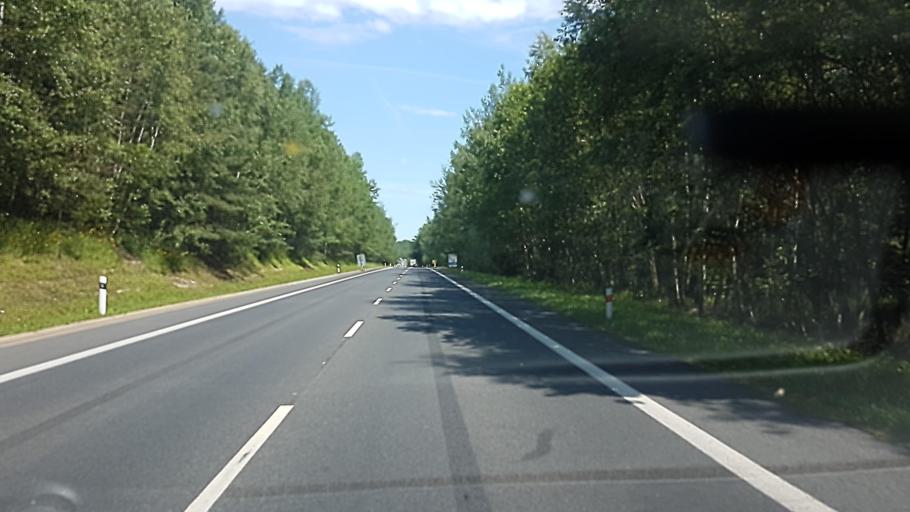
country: CZ
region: Karlovarsky
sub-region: Okres Cheb
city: Frantiskovy Lazne
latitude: 50.0976
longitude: 12.3069
